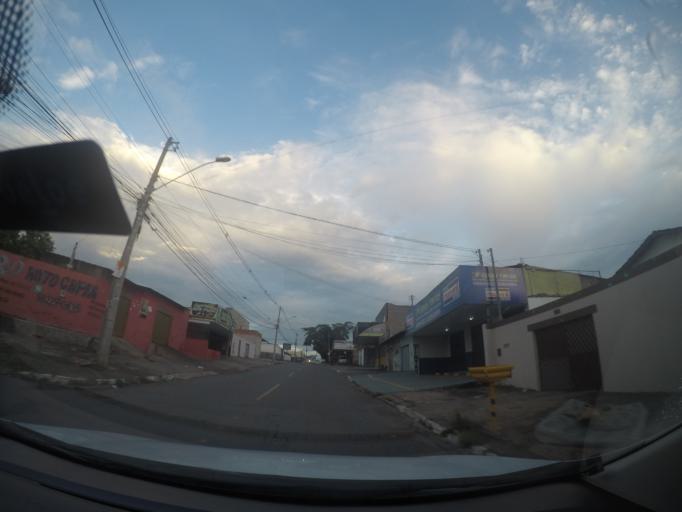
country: BR
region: Goias
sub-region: Goiania
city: Goiania
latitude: -16.7001
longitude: -49.3490
